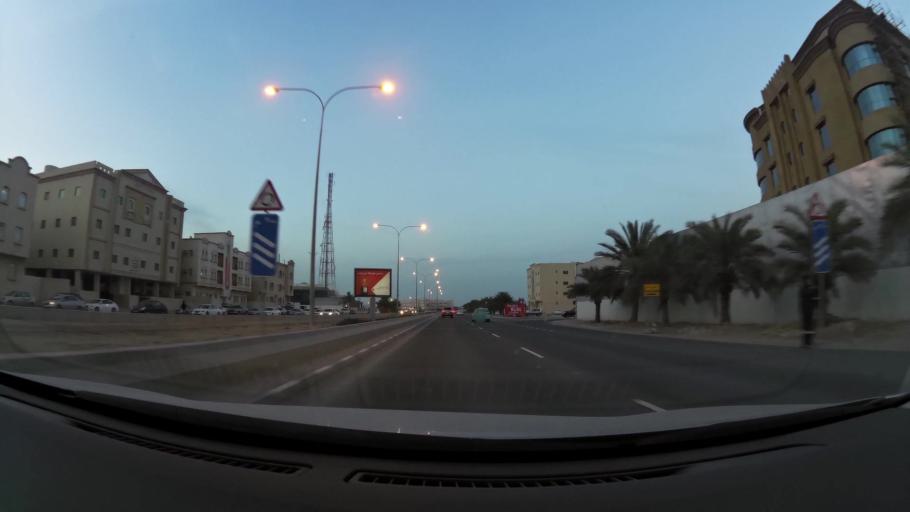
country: QA
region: Al Wakrah
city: Al Wakrah
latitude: 25.1587
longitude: 51.6062
